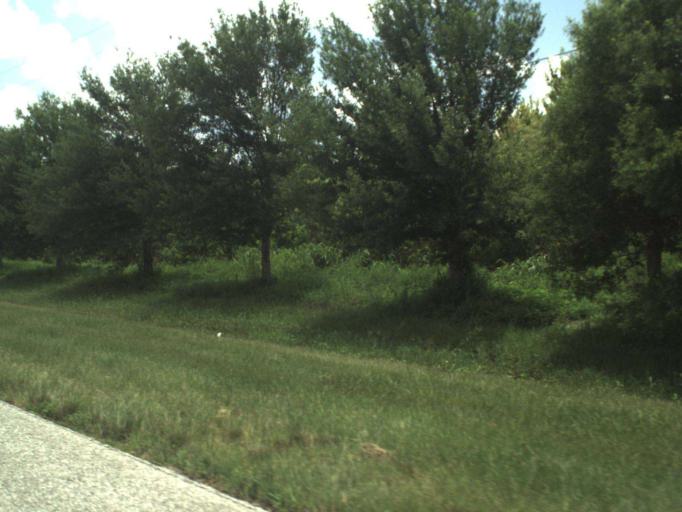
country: US
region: Florida
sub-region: Indian River County
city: Fellsmere
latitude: 27.6405
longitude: -80.6668
